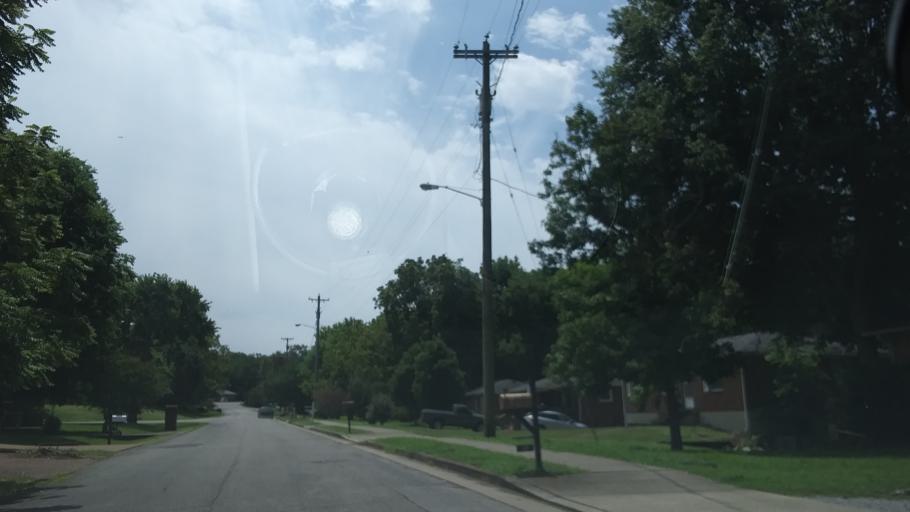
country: US
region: Tennessee
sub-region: Davidson County
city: Belle Meade
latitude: 36.1489
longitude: -86.8818
